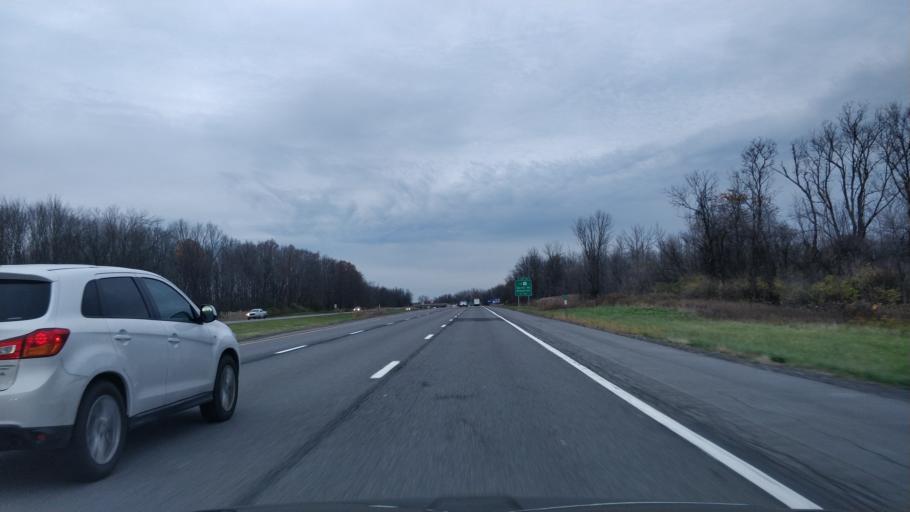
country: US
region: New York
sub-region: Onondaga County
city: Brewerton
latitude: 43.2228
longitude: -76.1293
